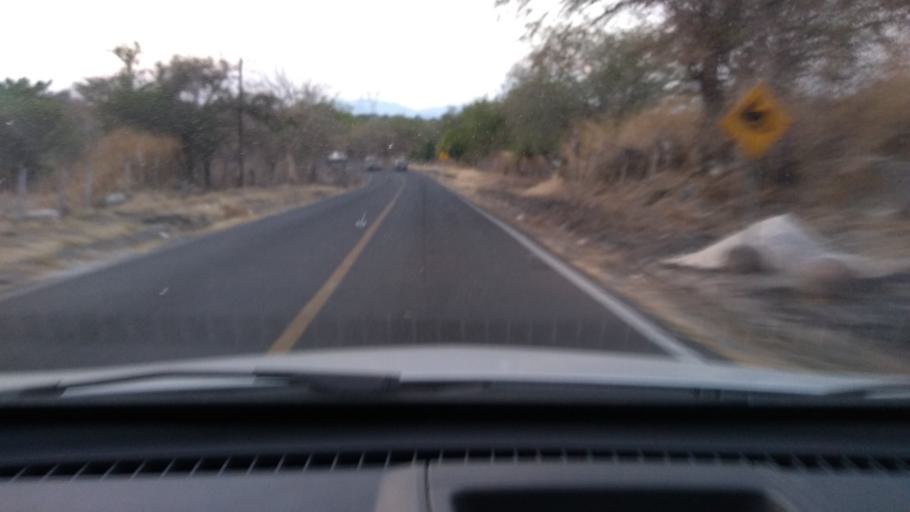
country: MX
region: Morelos
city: Coatetelco
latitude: 18.7240
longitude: -99.2952
